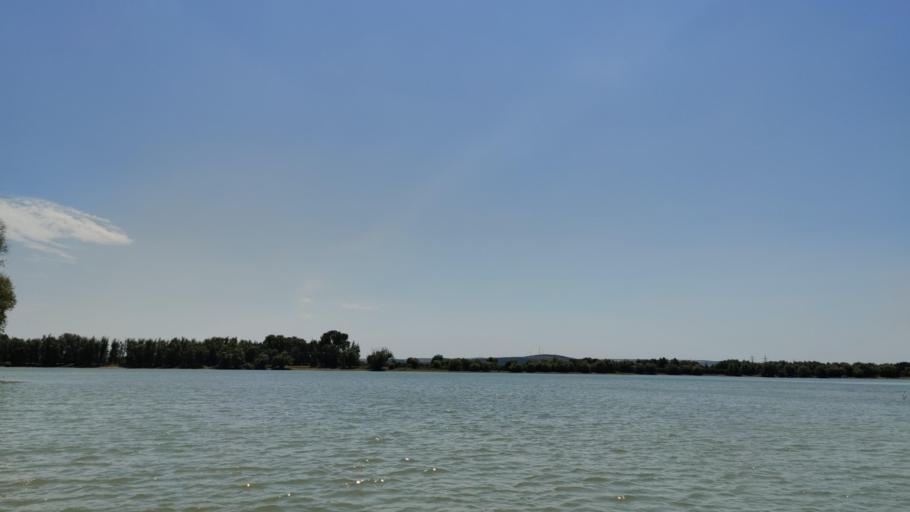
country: RO
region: Tulcea
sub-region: Municipiul Tulcea
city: Tulcea
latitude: 45.2049
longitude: 28.8527
